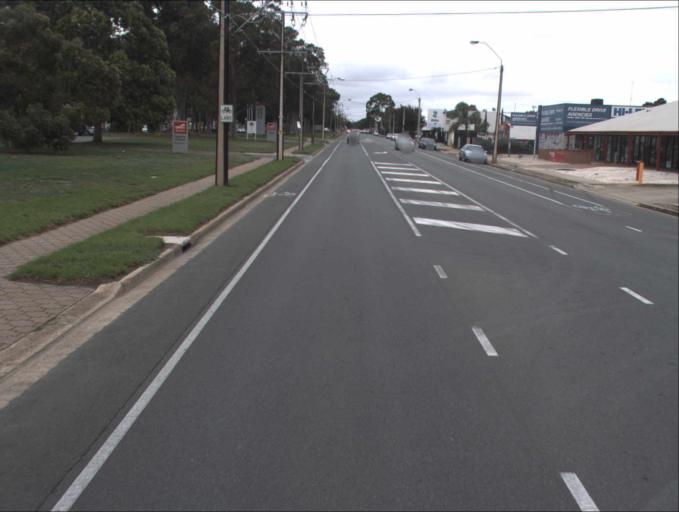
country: AU
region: South Australia
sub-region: Charles Sturt
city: Woodville
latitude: -34.8715
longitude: 138.5661
